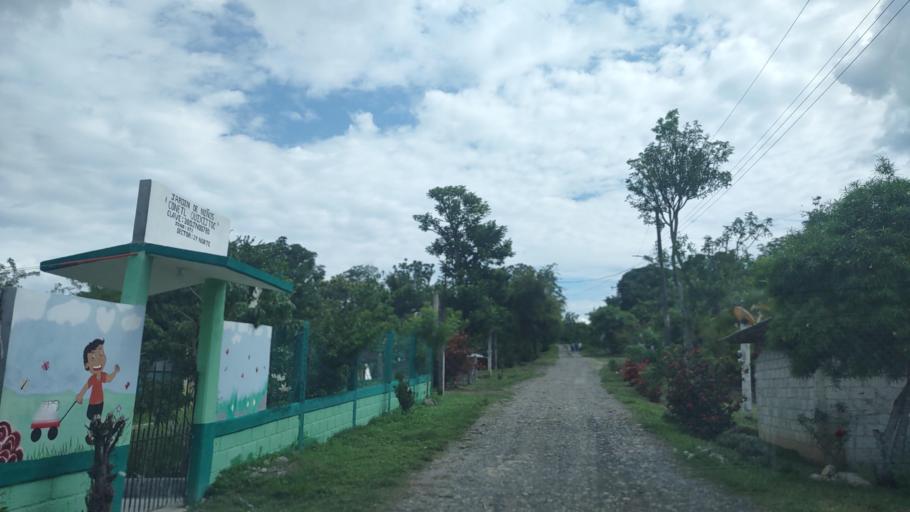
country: MX
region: Veracruz
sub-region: Ixcatepec
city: Ixcatepec
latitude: 21.2148
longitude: -97.9843
